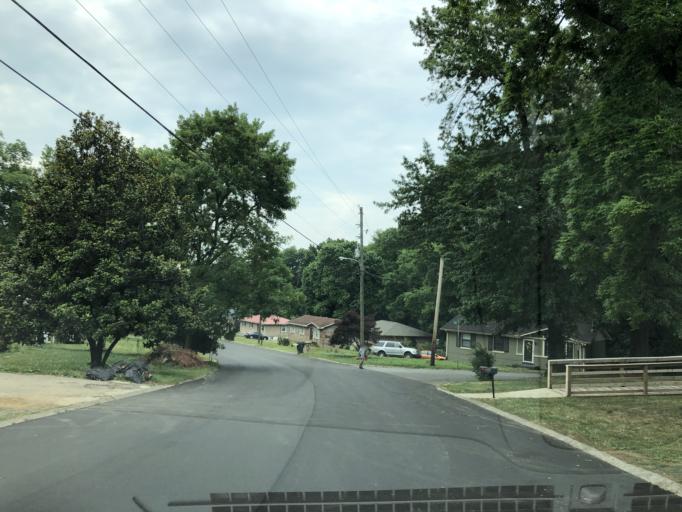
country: US
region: Tennessee
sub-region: Davidson County
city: Oak Hill
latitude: 36.0767
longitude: -86.6848
